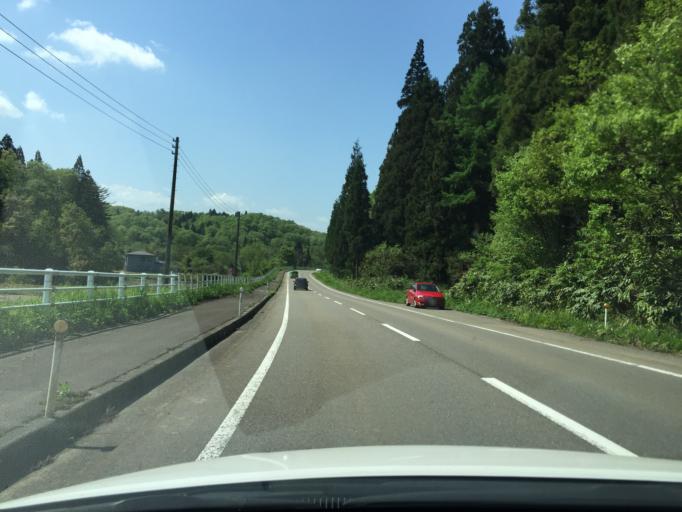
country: JP
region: Niigata
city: Kamo
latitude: 37.5797
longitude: 139.0932
